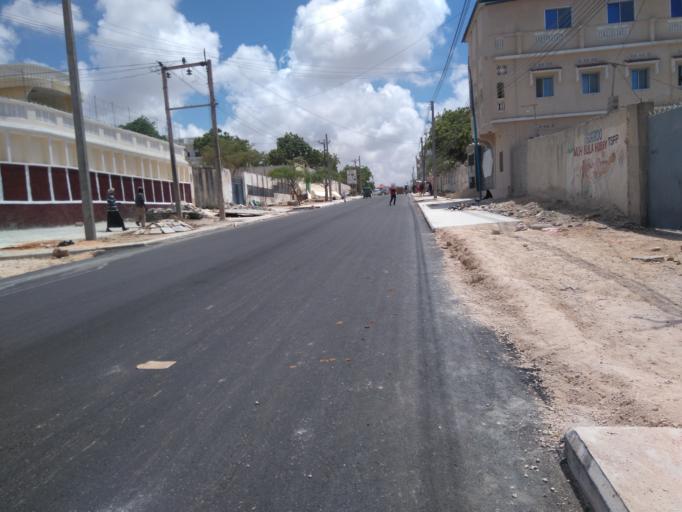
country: SO
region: Banaadir
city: Mogadishu
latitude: 2.0293
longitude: 45.3028
